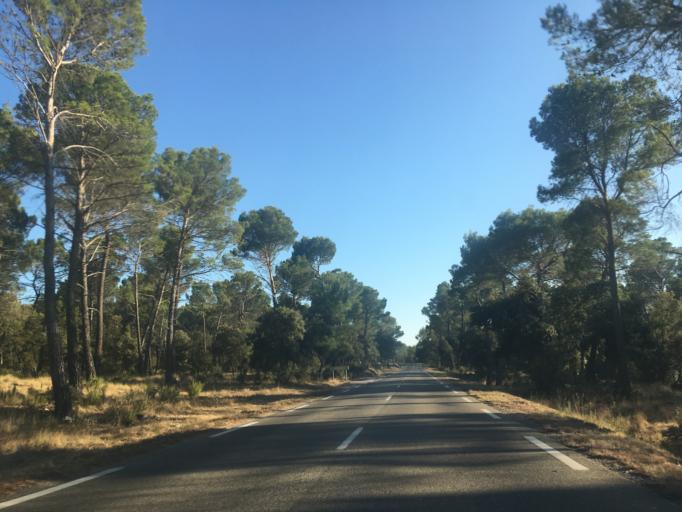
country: FR
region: Provence-Alpes-Cote d'Azur
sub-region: Departement du Var
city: Villecroze
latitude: 43.5920
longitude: 6.2572
